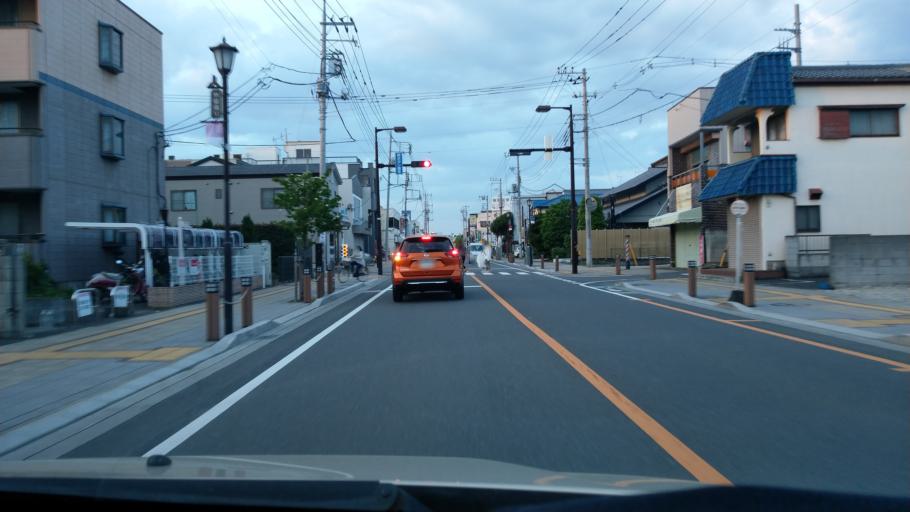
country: JP
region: Saitama
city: Iwatsuki
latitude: 35.9466
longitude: 139.6941
